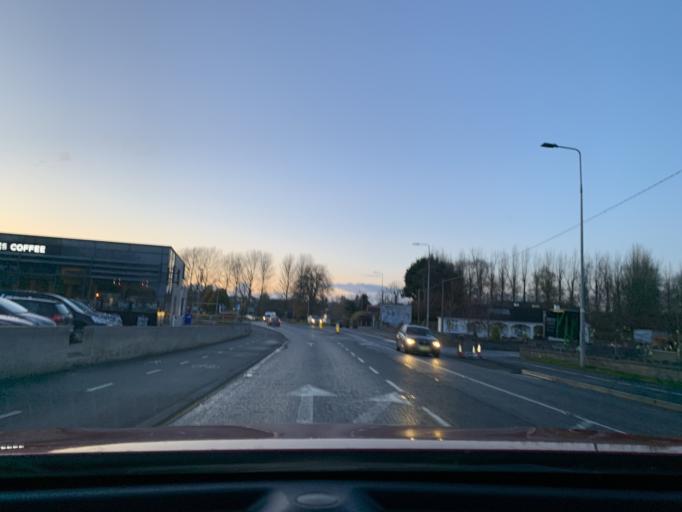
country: IE
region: Connaught
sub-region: County Leitrim
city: Carrick-on-Shannon
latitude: 53.9460
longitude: -8.0773
